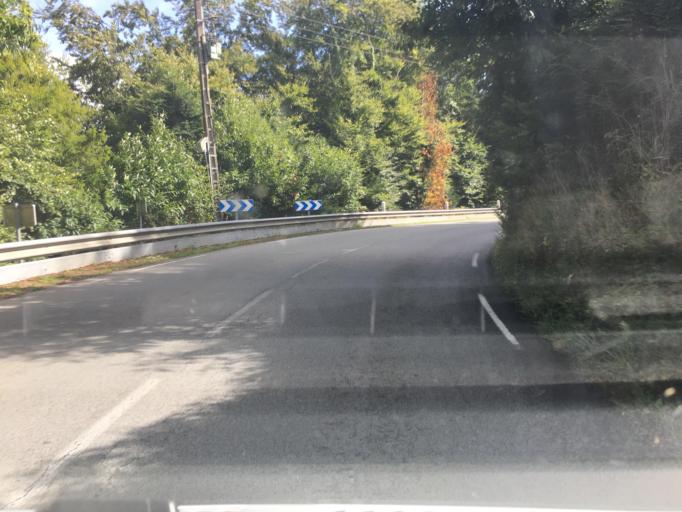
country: FR
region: Brittany
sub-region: Departement du Finistere
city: La Foret-Fouesnant
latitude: 47.9169
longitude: -3.9708
